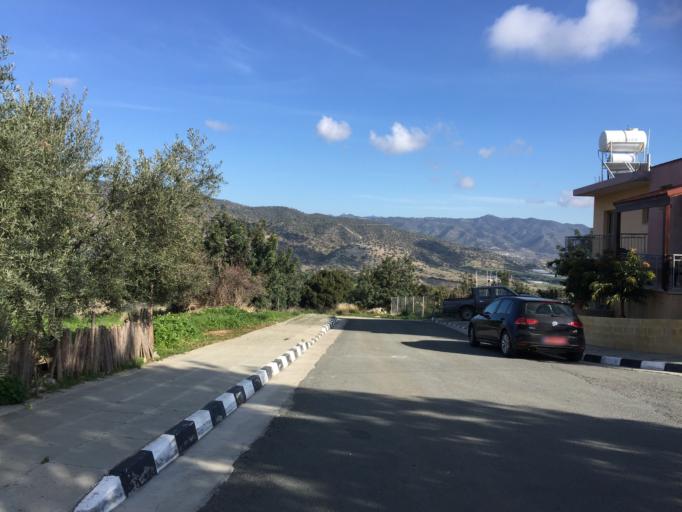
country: CY
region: Larnaka
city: Agios Tychon
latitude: 34.7452
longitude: 33.1283
